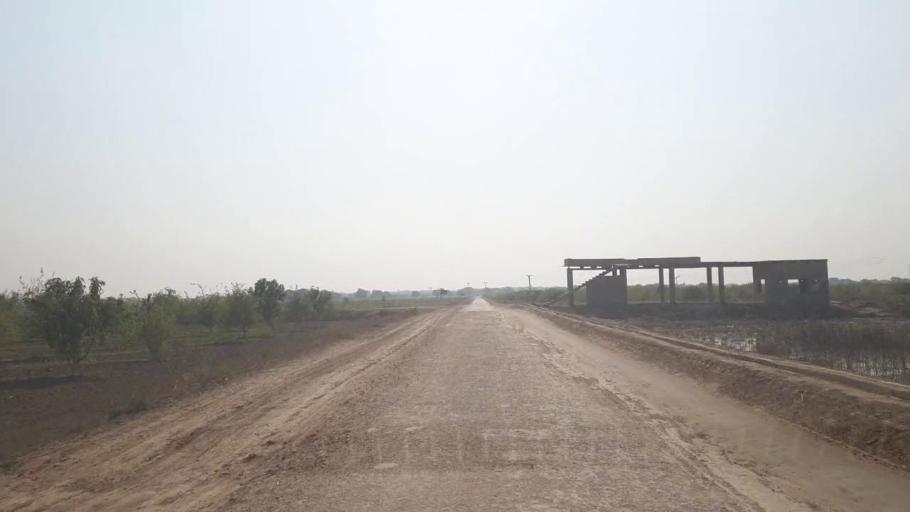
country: PK
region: Sindh
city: Tando Allahyar
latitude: 25.4622
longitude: 68.8143
